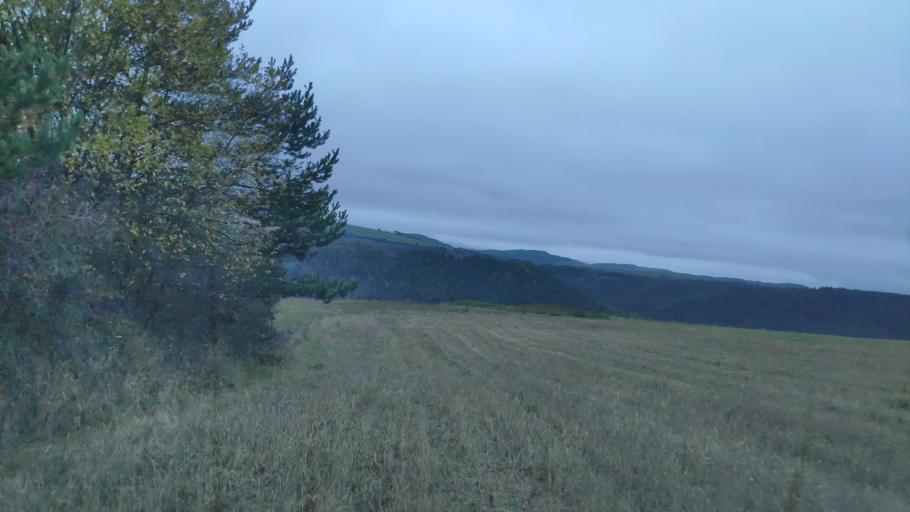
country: SK
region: Presovsky
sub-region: Okres Presov
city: Presov
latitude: 48.9369
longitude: 21.0858
